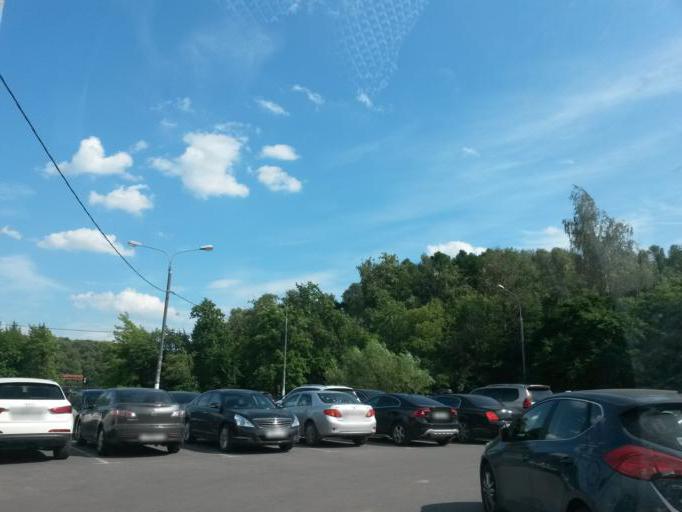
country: RU
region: Moscow
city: Orekhovo-Borisovo Severnoye
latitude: 55.6150
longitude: 37.6735
